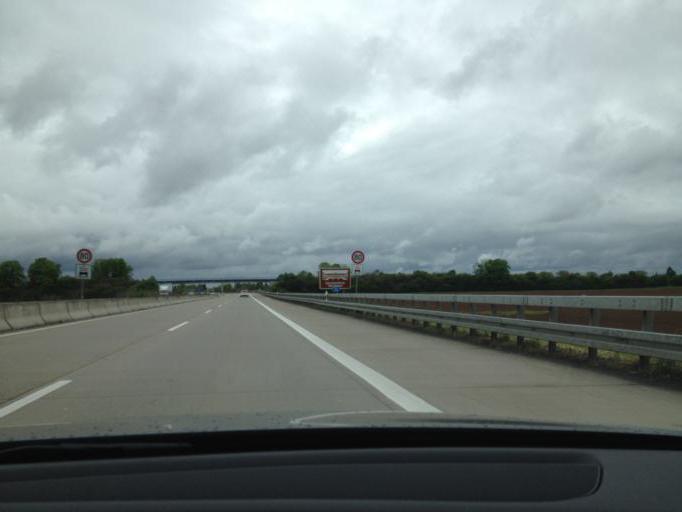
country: DE
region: Baden-Wuerttemberg
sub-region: Karlsruhe Region
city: Edingen-Neckarhausen
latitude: 49.4387
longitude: 8.5982
